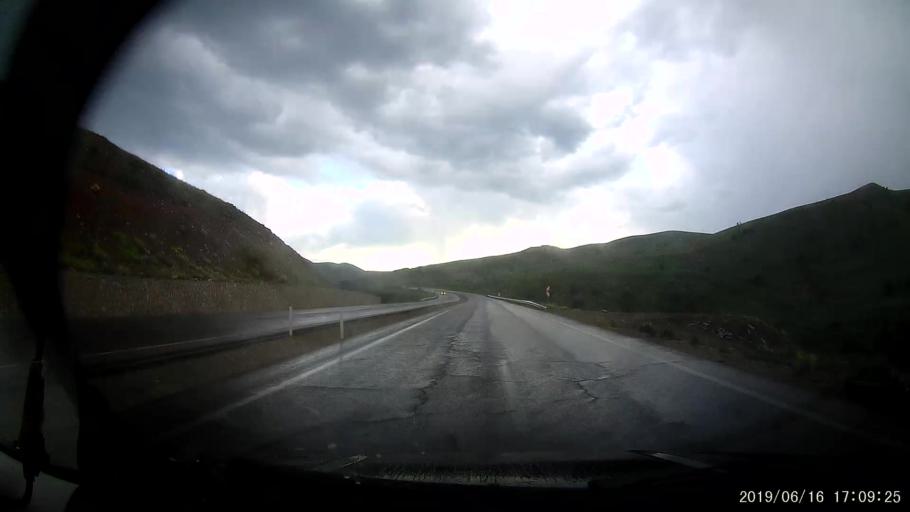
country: TR
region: Erzurum
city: Askale
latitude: 39.8954
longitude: 40.6496
